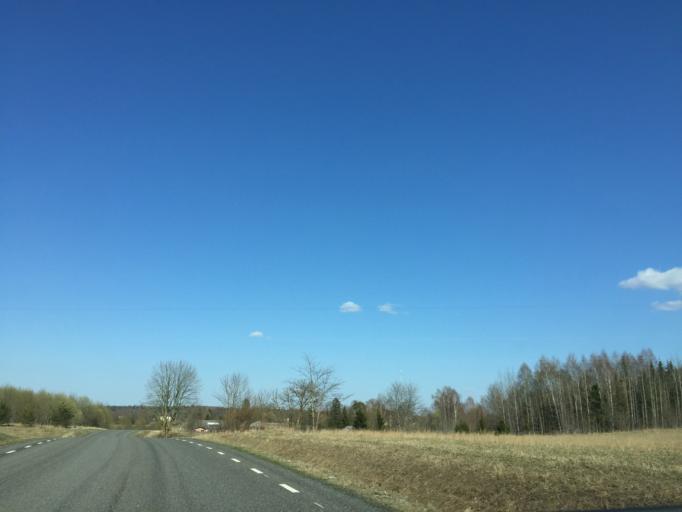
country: EE
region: Viljandimaa
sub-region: Viiratsi vald
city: Viiratsi
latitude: 58.2708
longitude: 25.6793
